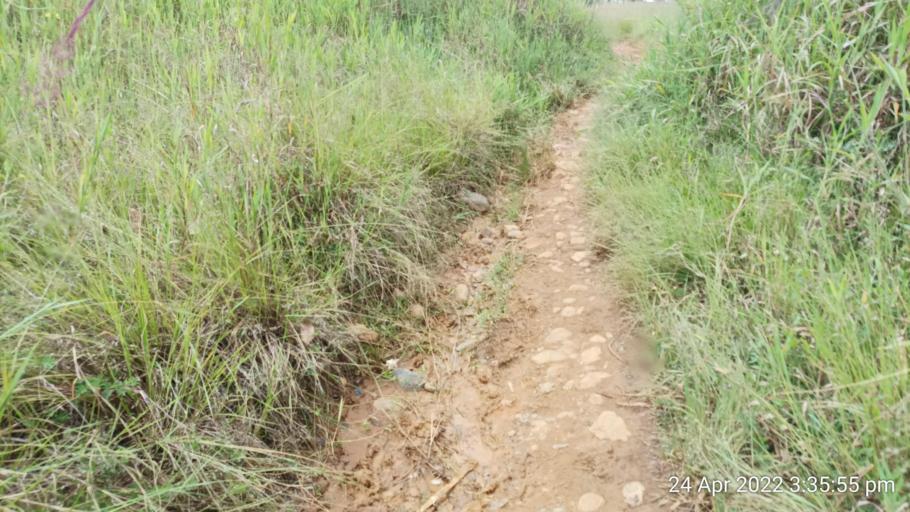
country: PG
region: Jiwaka
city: Minj
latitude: -5.8922
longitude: 144.8205
